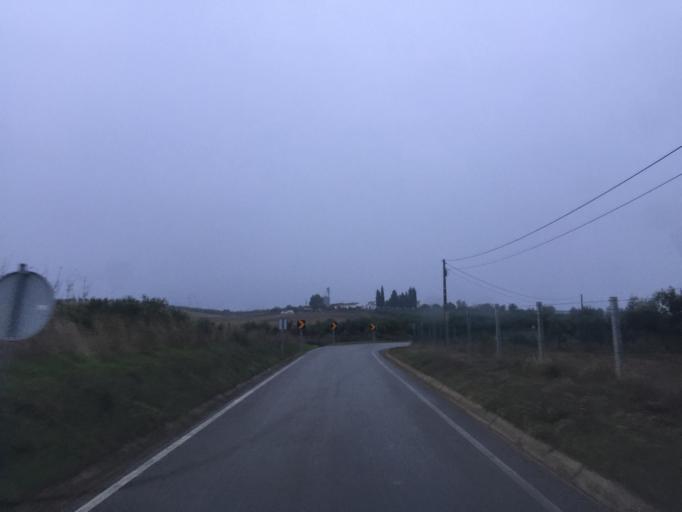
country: PT
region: Portalegre
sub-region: Avis
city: Avis
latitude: 39.0460
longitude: -7.9067
